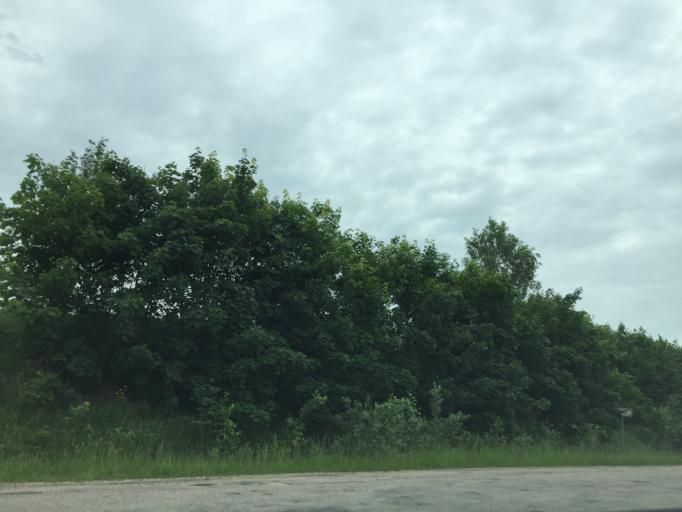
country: LV
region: Tukuma Rajons
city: Tukums
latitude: 57.0444
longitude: 23.1234
